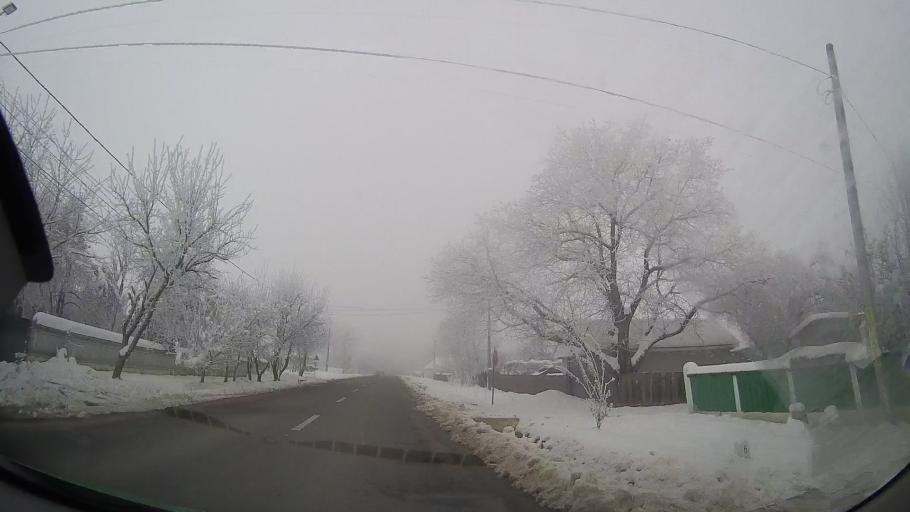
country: RO
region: Iasi
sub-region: Comuna Mogosesti-Siret
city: Mogosesti-Siret
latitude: 47.1628
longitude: 26.7716
